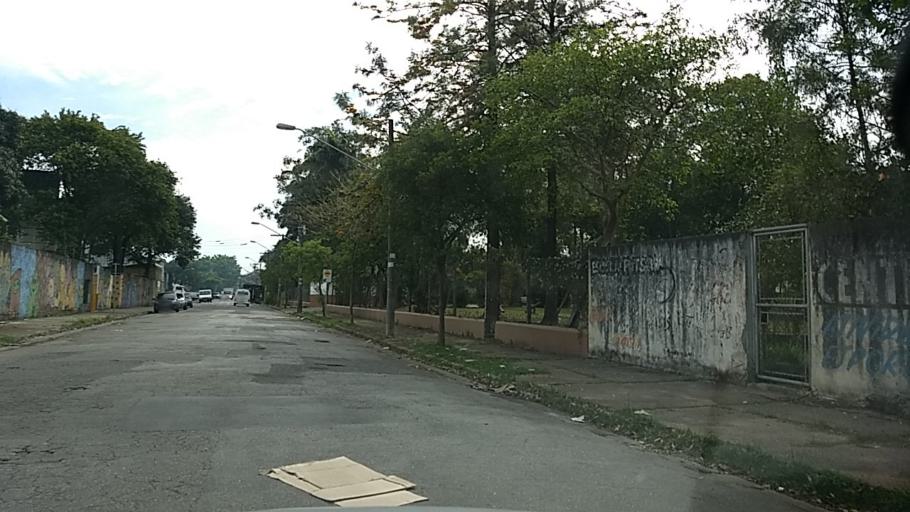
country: BR
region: Sao Paulo
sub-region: Guarulhos
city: Guarulhos
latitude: -23.5005
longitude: -46.5699
